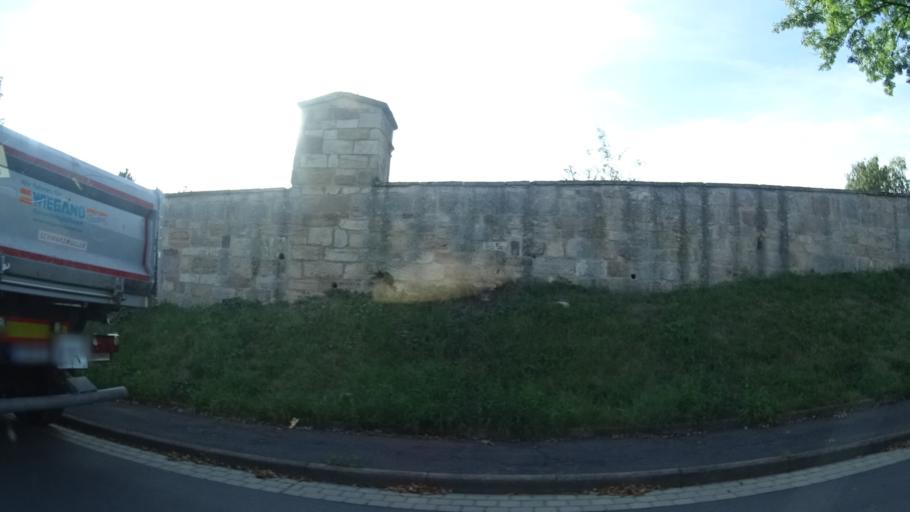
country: DE
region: Hesse
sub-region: Regierungsbezirk Kassel
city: Flieden
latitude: 50.4280
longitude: 9.5685
